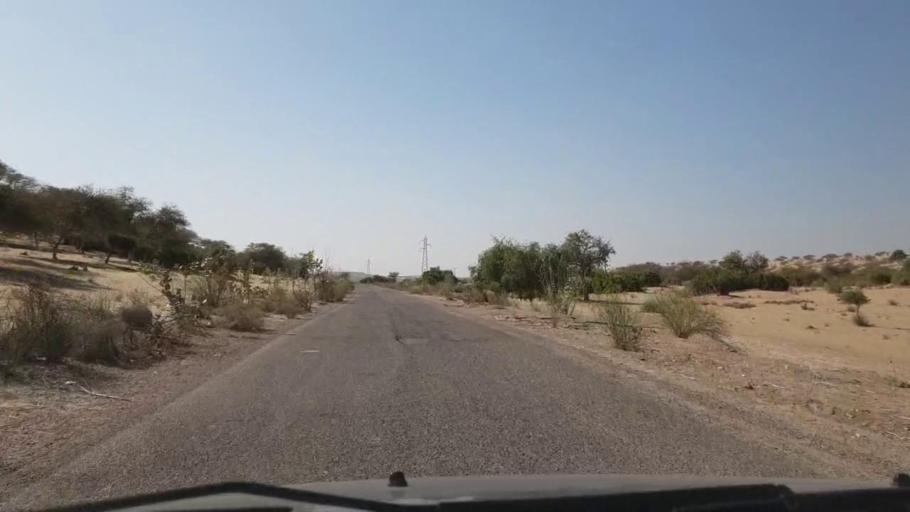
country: PK
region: Sindh
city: Diplo
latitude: 24.5763
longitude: 69.6929
